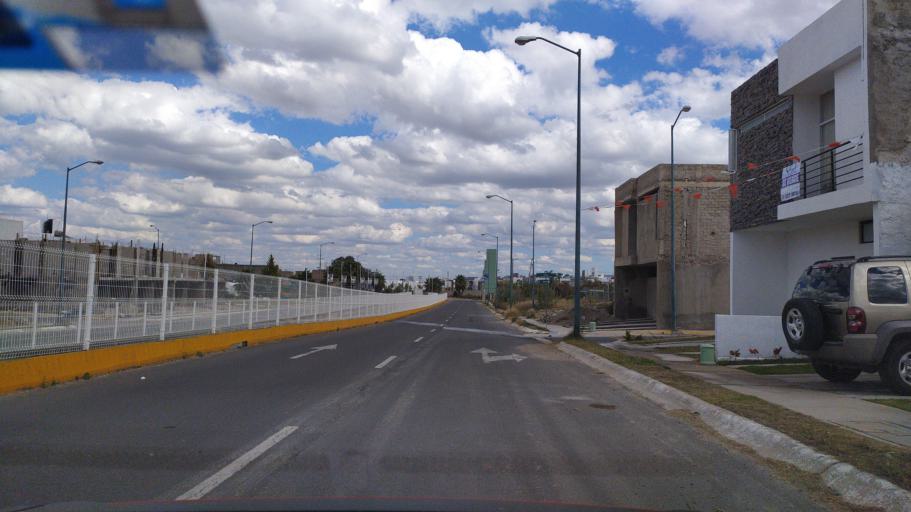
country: MX
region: Jalisco
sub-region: Tlajomulco de Zuniga
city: Palomar
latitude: 20.6314
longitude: -103.4786
